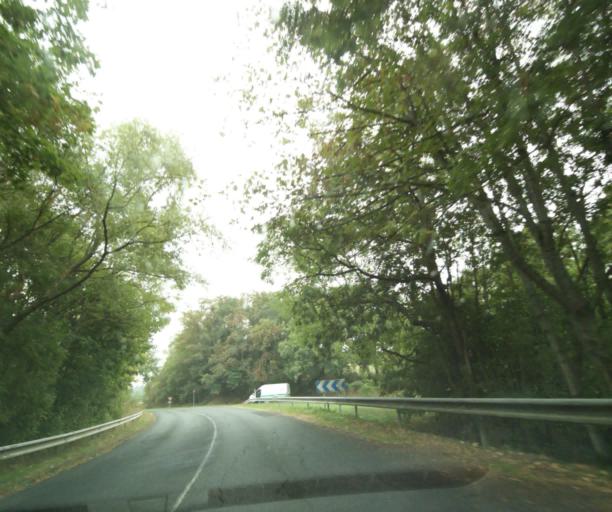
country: FR
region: Auvergne
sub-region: Departement du Puy-de-Dome
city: Ceyrat
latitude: 45.7188
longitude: 3.0680
